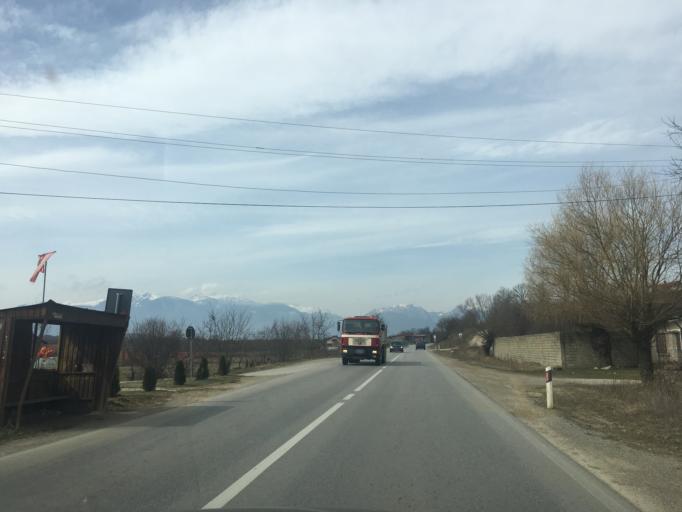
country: XK
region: Pec
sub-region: Komuna e Pejes
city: Kosuriq
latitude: 42.6165
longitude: 20.4945
